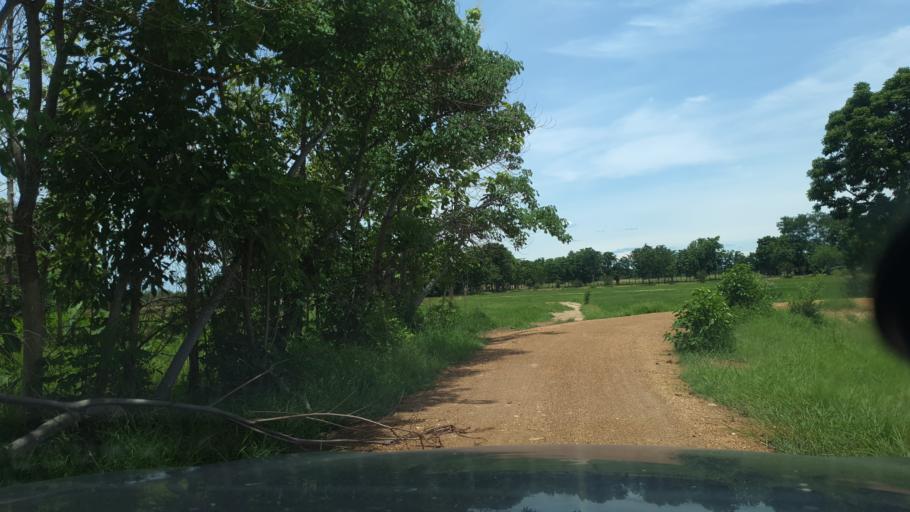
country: TH
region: Sukhothai
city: Ban Na
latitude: 17.0753
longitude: 99.6950
